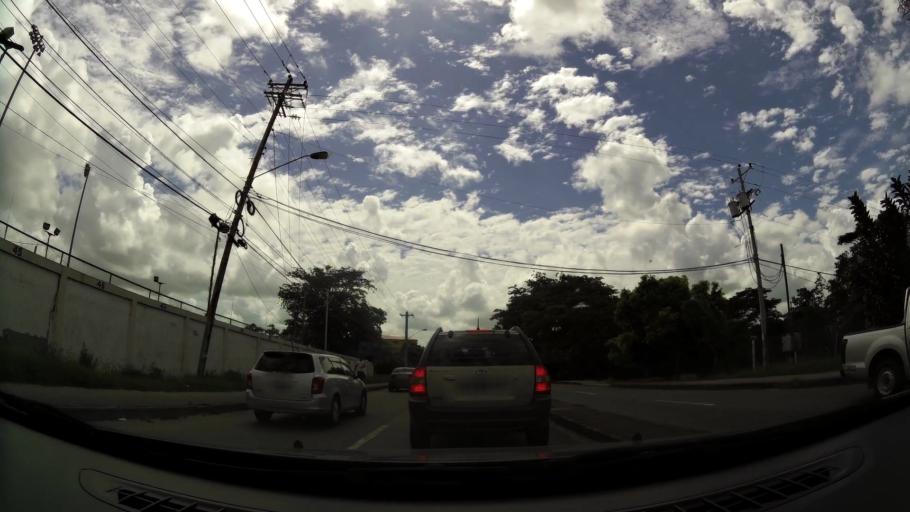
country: TT
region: City of San Fernando
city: Marabella
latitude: 10.3099
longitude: -61.4524
